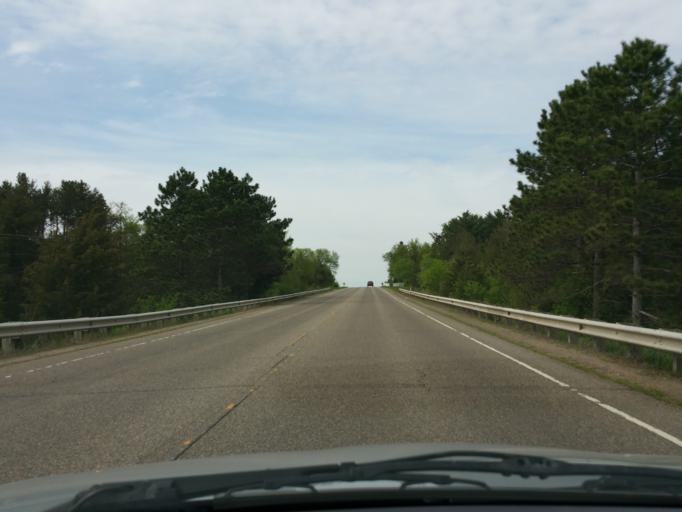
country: US
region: Wisconsin
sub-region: Saint Croix County
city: Hudson
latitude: 44.9538
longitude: -92.6905
